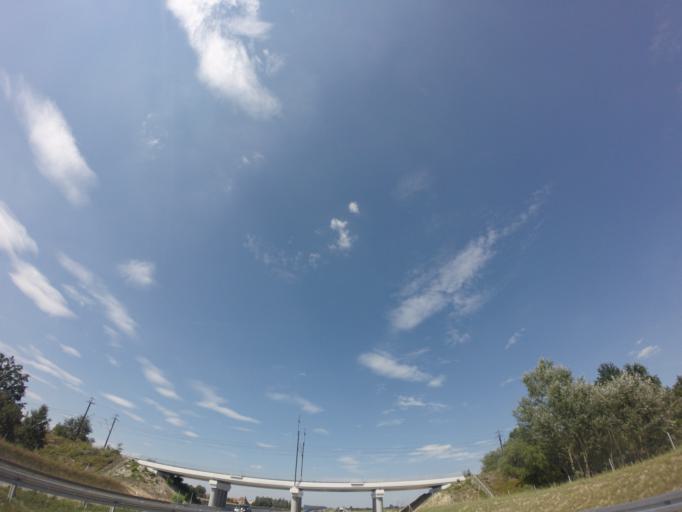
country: PL
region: Lower Silesian Voivodeship
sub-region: Legnica
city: Legnica
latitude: 51.2300
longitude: 16.1416
